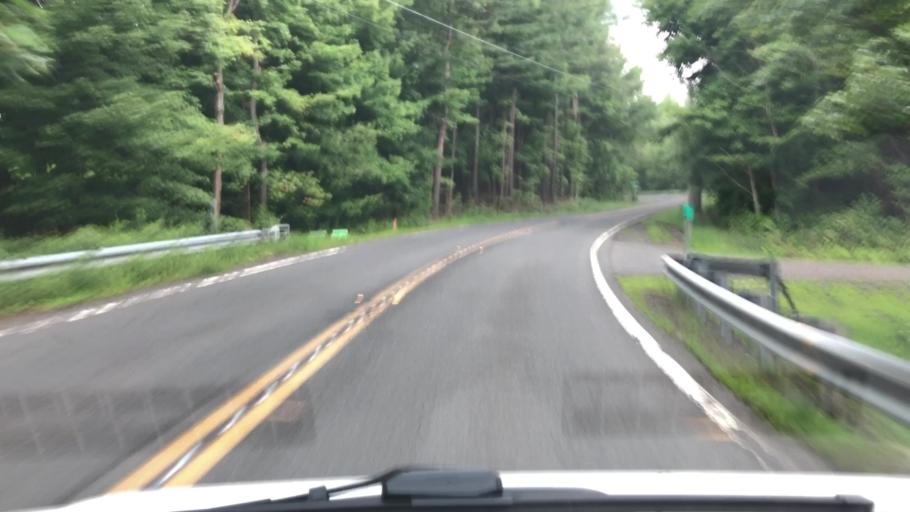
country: US
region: Massachusetts
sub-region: Franklin County
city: Conway
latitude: 42.5114
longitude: -72.6667
